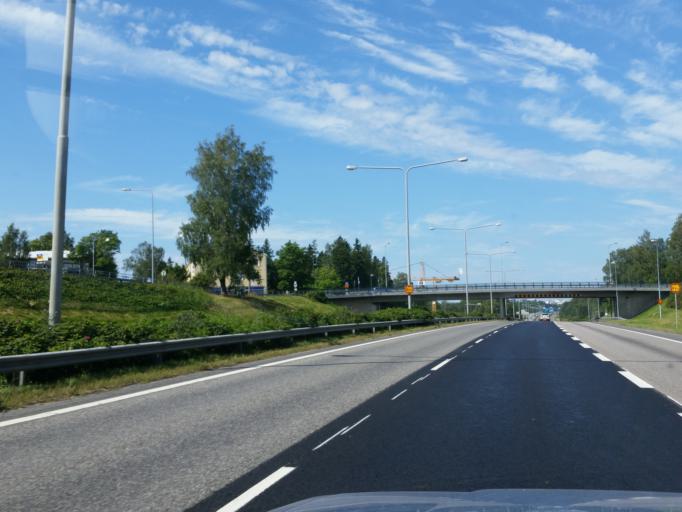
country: FI
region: Uusimaa
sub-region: Helsinki
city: Teekkarikylae
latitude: 60.1628
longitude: 24.8619
